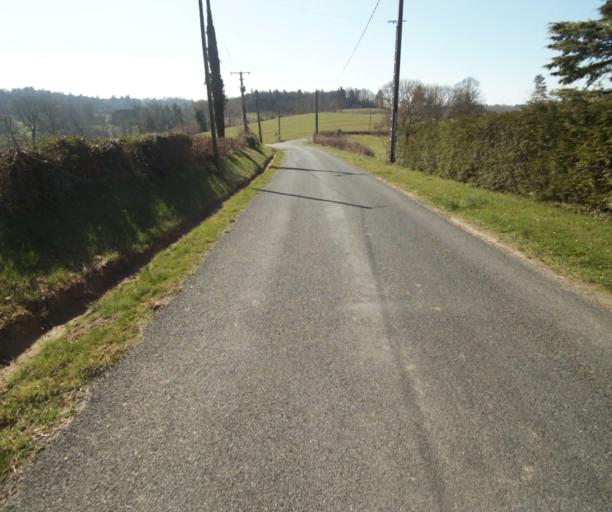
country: FR
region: Limousin
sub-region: Departement de la Correze
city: Saint-Mexant
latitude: 45.2953
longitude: 1.6152
